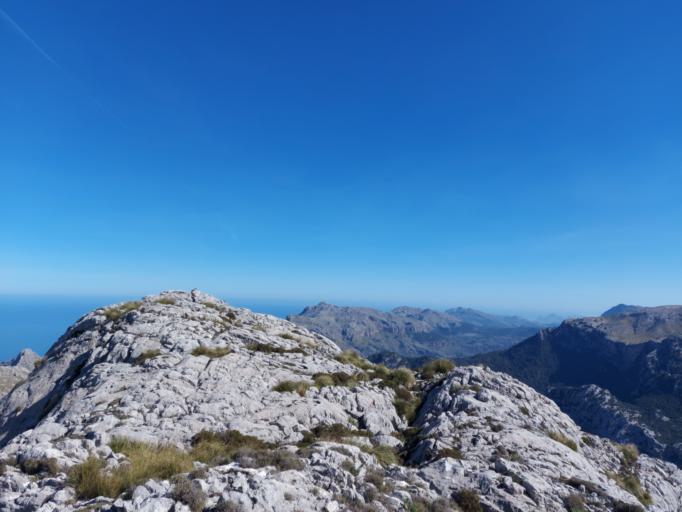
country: ES
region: Balearic Islands
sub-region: Illes Balears
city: Escorca
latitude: 39.8054
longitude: 2.8091
